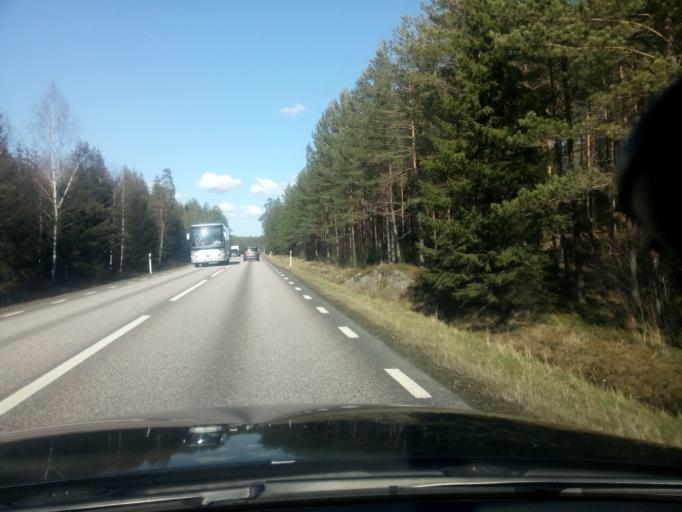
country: SE
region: Soedermanland
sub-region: Strangnas Kommun
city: Akers Styckebruk
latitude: 59.2215
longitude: 16.9111
